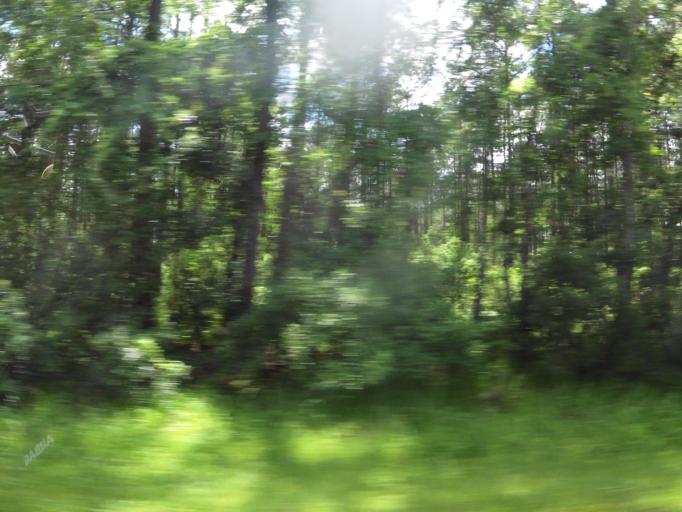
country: US
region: Florida
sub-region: Clay County
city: Green Cove Springs
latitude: 29.9878
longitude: -81.7313
